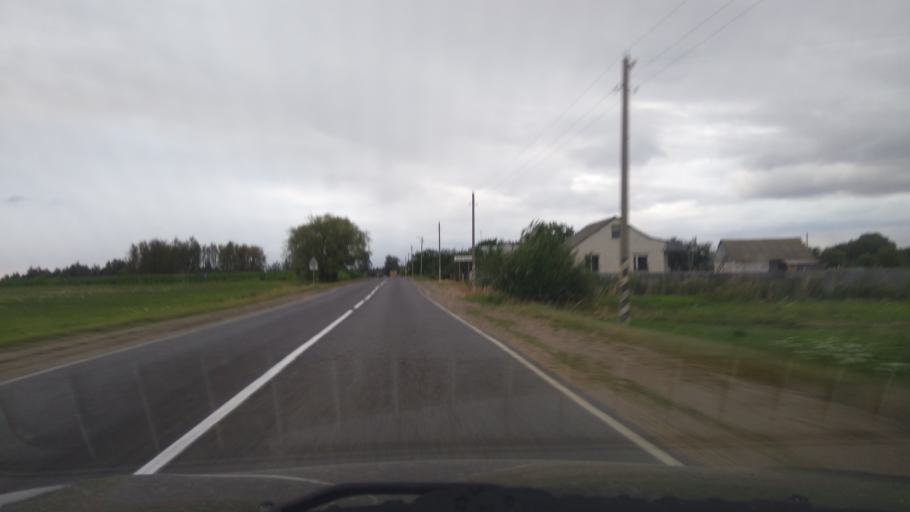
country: BY
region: Brest
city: Byaroza
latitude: 52.4522
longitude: 24.9700
